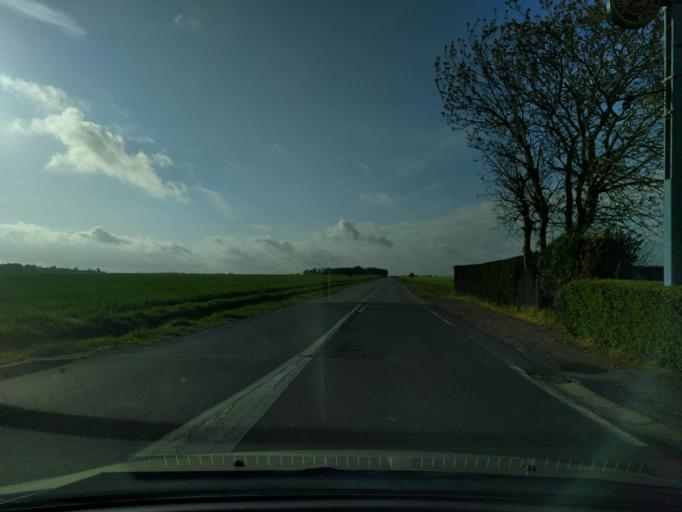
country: FR
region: Haute-Normandie
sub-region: Departement de l'Eure
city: Damville
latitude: 48.9077
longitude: 1.0224
